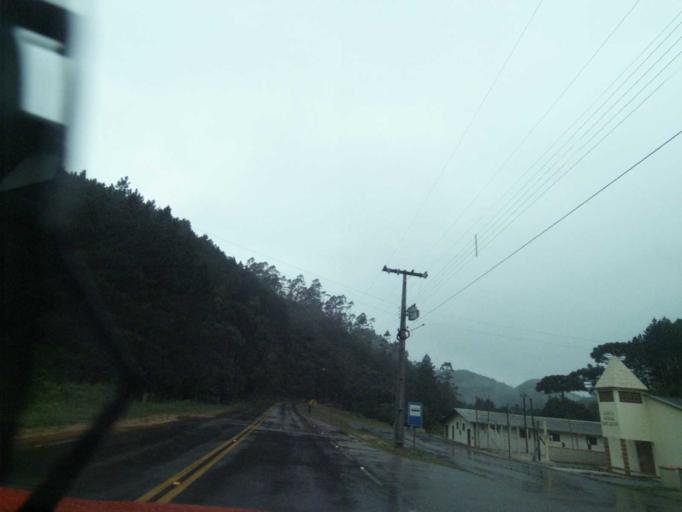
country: BR
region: Santa Catarina
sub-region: Anitapolis
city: Anitapolis
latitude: -27.8360
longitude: -49.0523
